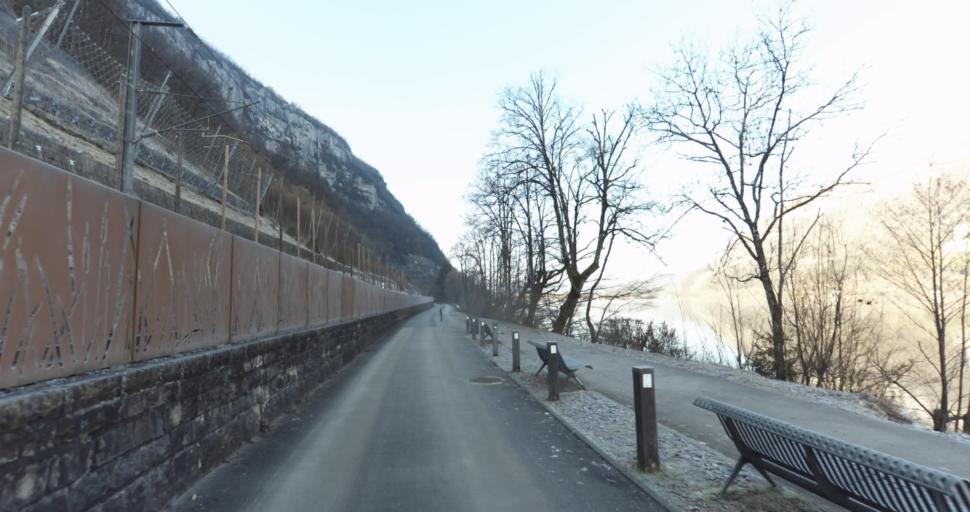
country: FR
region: Rhone-Alpes
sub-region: Departement de l'Ain
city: Nantua
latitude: 46.1574
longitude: 5.5908
